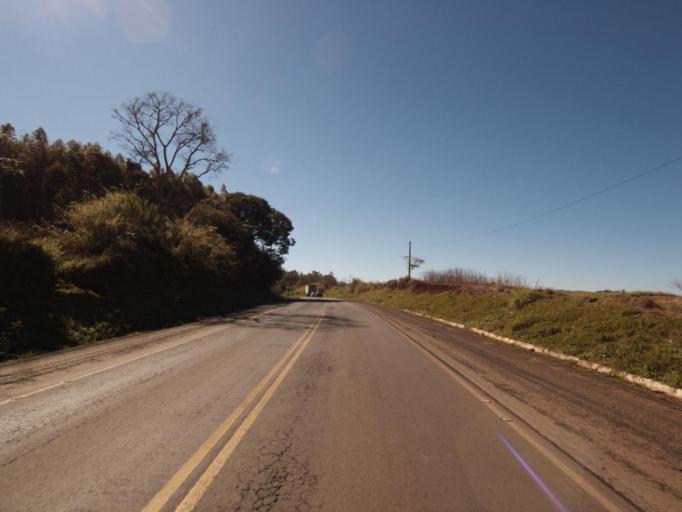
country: BR
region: Rio Grande do Sul
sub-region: Frederico Westphalen
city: Frederico Westphalen
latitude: -26.9161
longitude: -53.1899
